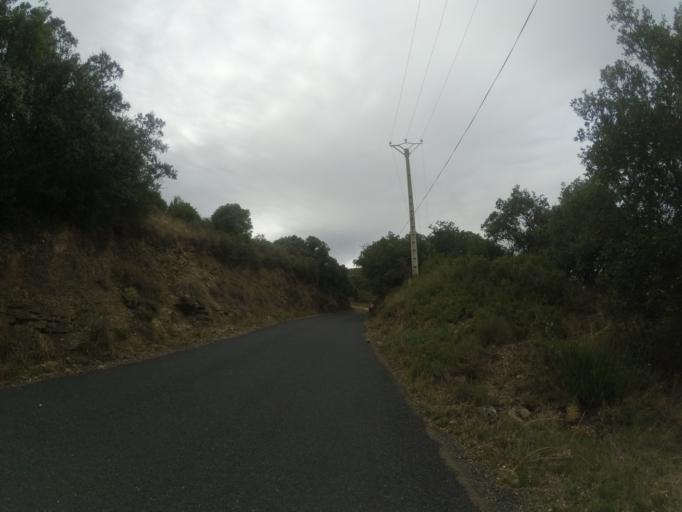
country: FR
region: Languedoc-Roussillon
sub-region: Departement des Pyrenees-Orientales
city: Corneilla-la-Riviere
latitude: 42.7320
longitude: 2.7350
